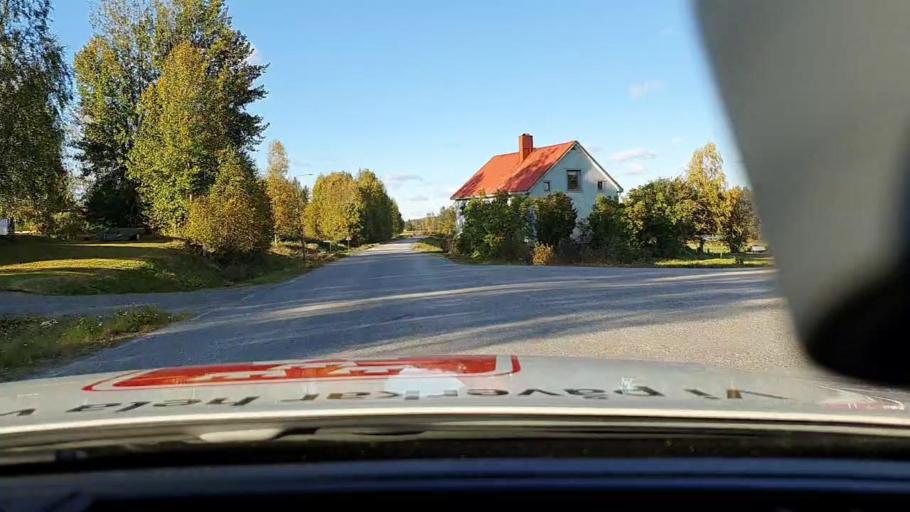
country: SE
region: Norrbotten
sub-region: Pitea Kommun
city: Norrfjarden
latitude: 65.5171
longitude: 21.4950
